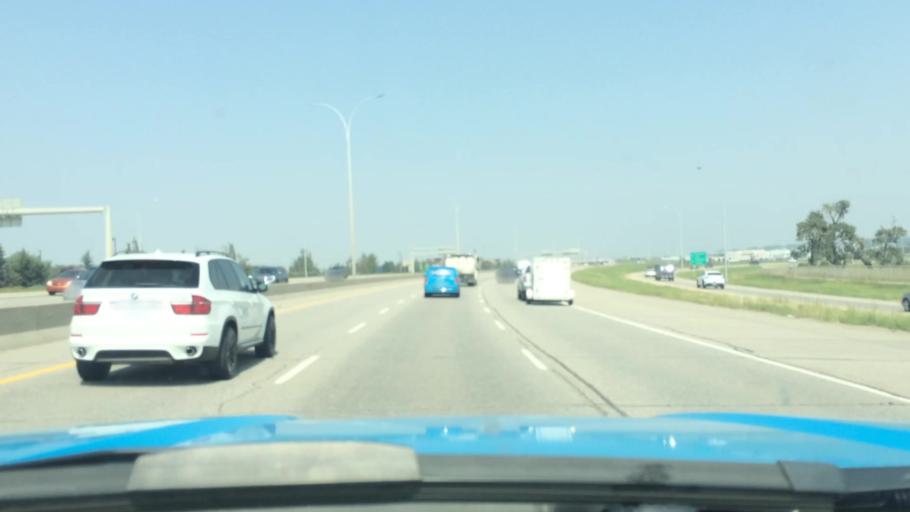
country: CA
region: Alberta
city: Calgary
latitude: 50.9778
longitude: -114.0403
